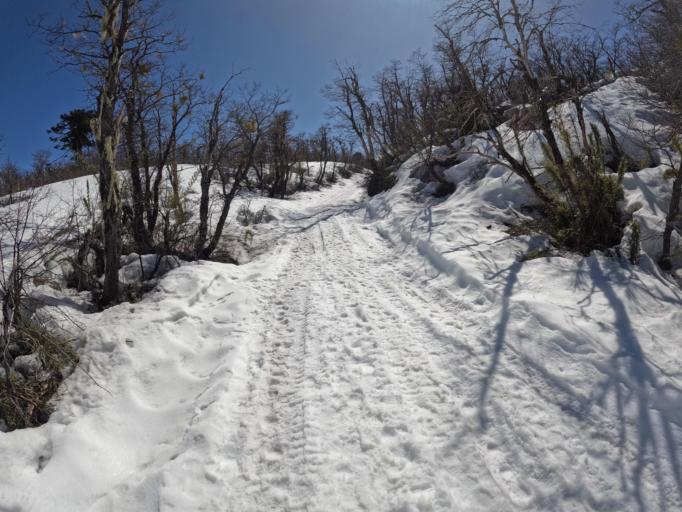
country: CL
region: Araucania
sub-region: Provincia de Cautin
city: Vilcun
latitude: -38.6605
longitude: -71.6187
